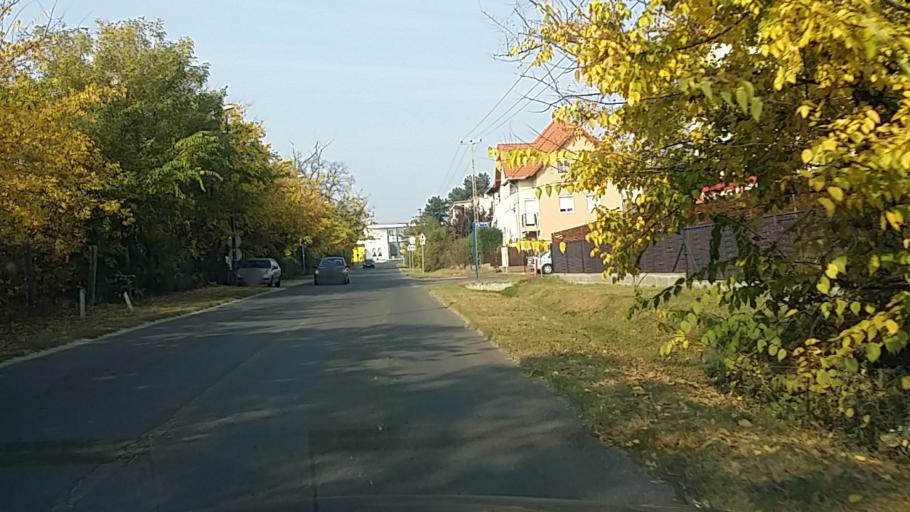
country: HU
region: Pest
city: Dunakeszi
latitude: 47.6170
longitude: 19.1555
